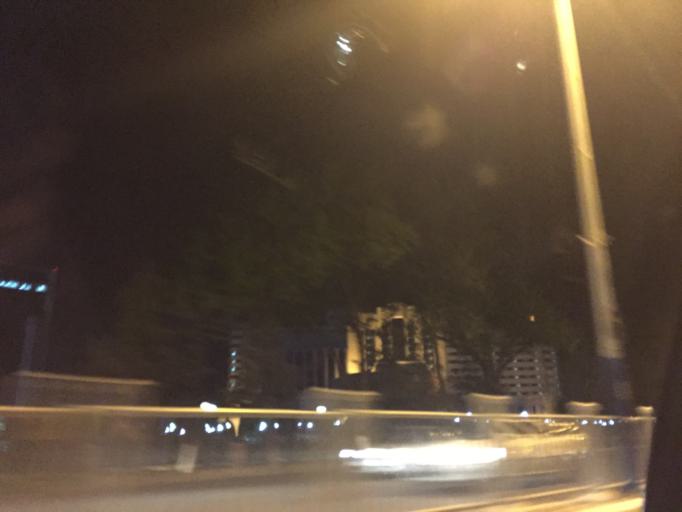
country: UZ
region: Toshkent Shahri
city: Tashkent
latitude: 41.3360
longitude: 69.2850
